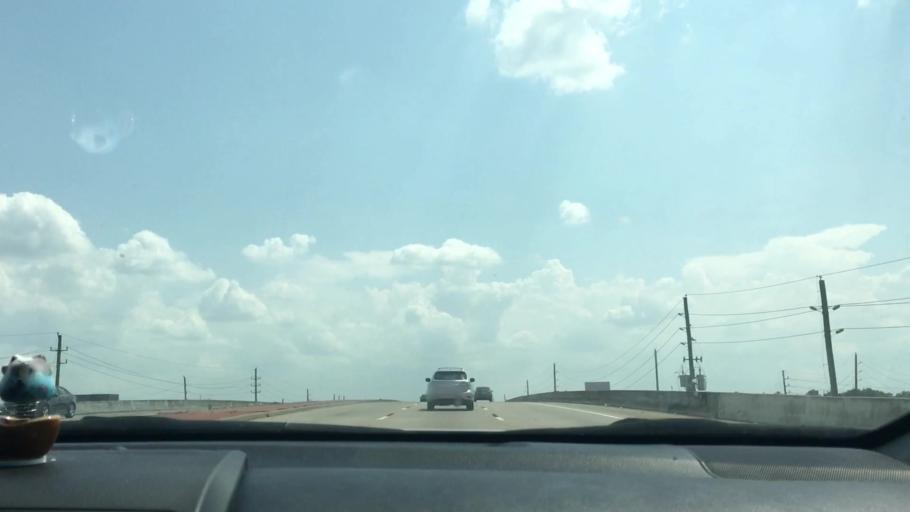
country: US
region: Texas
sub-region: Fort Bend County
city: Mission Bend
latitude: 29.7120
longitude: -95.6442
